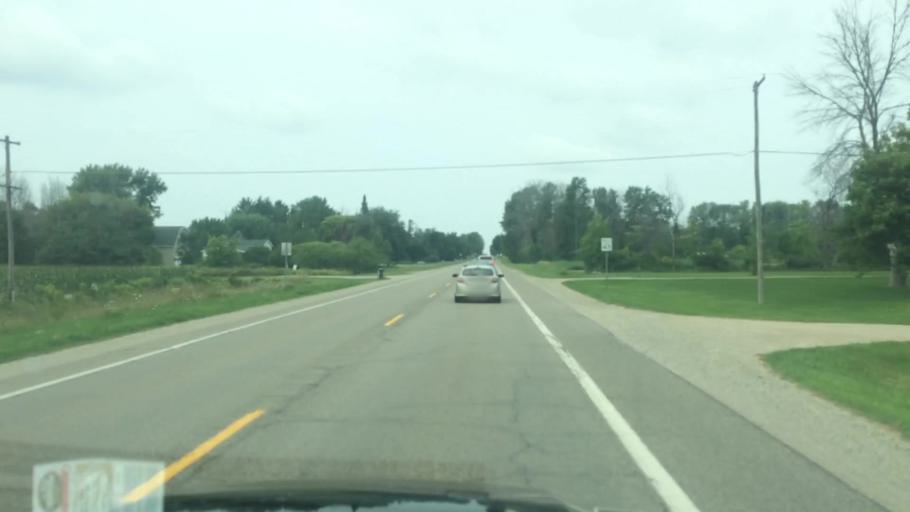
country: US
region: Michigan
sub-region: Huron County
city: Bad Axe
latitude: 43.8892
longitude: -83.0031
